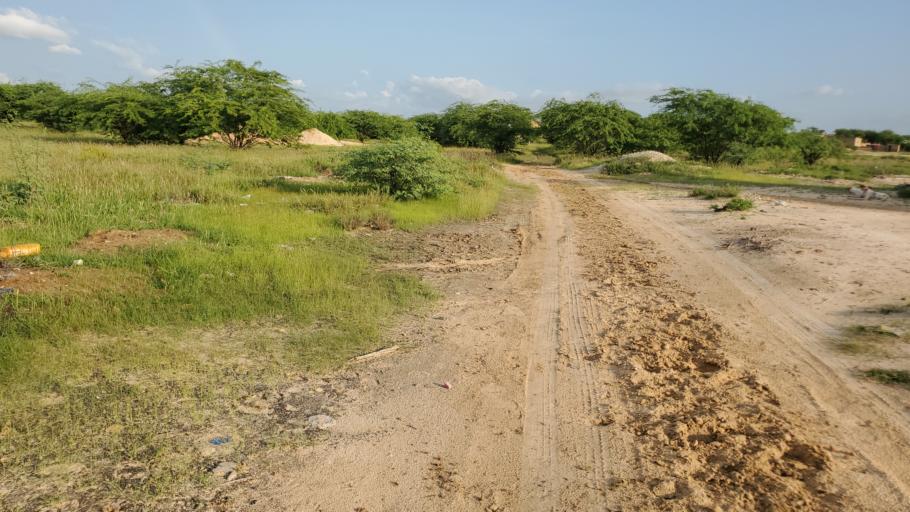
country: SN
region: Saint-Louis
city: Saint-Louis
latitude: 16.0505
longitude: -16.4200
